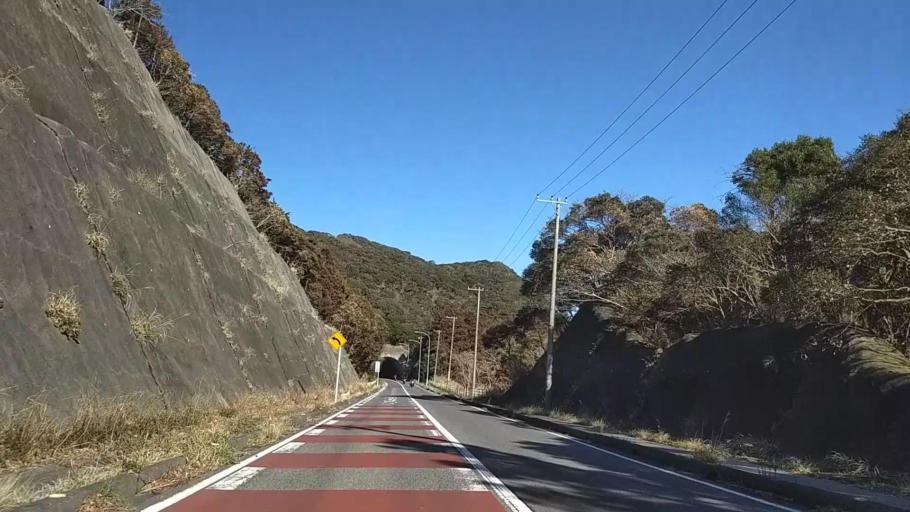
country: JP
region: Chiba
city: Katsuura
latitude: 35.1282
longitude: 140.2384
